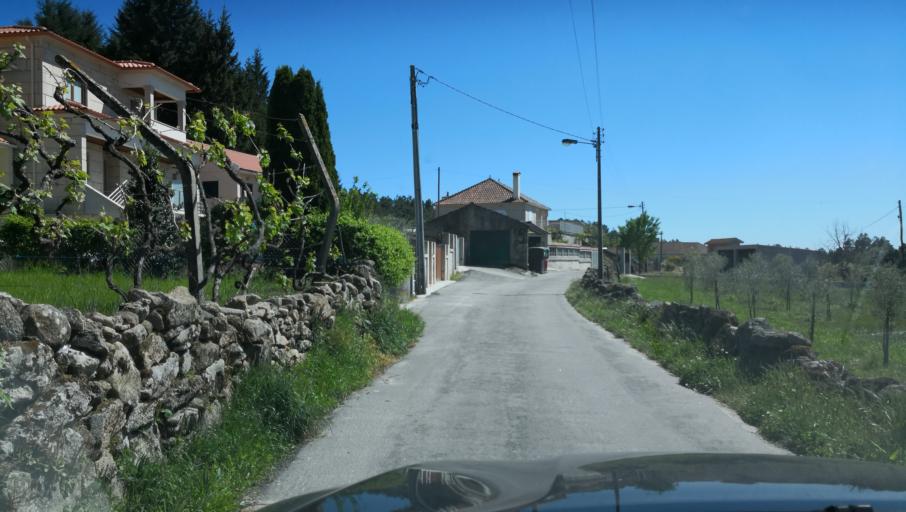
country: PT
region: Vila Real
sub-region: Vila Real
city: Vila Real
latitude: 41.2975
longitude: -7.6590
